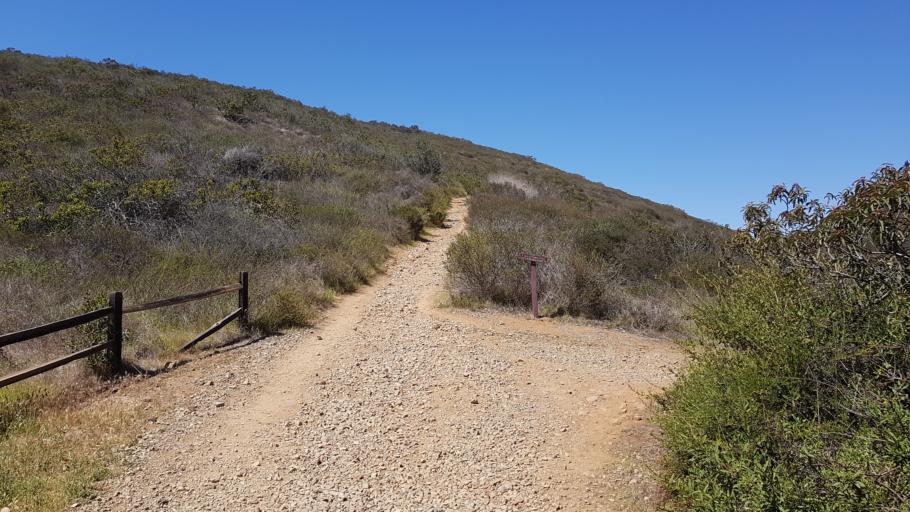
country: US
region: California
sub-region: San Diego County
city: Poway
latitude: 32.9758
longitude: -117.1110
